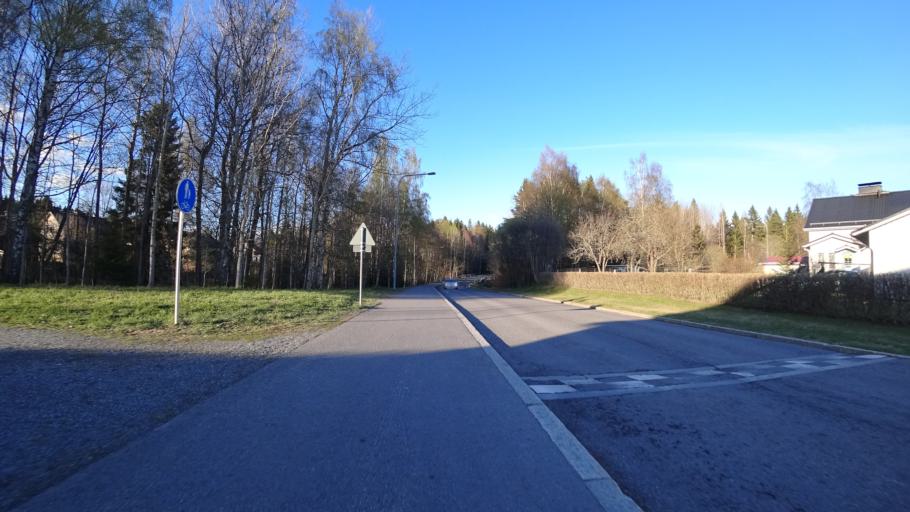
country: FI
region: Pirkanmaa
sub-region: Tampere
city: Pirkkala
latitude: 61.4974
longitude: 23.5884
